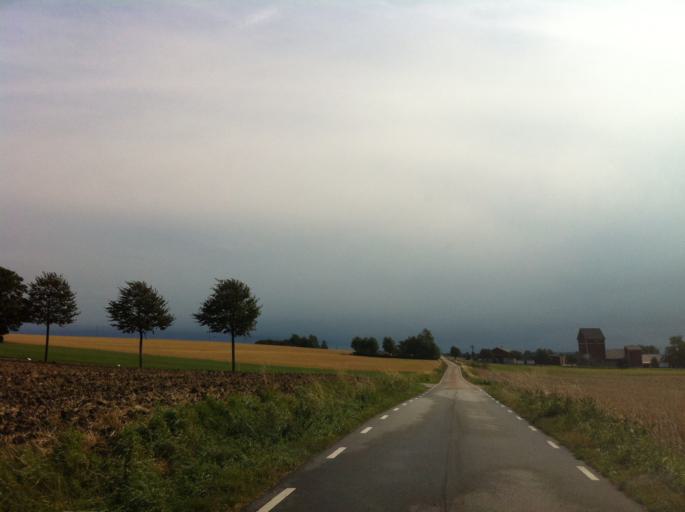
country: SE
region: Skane
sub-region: Landskrona
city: Landskrona
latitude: 55.9163
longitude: 12.8732
